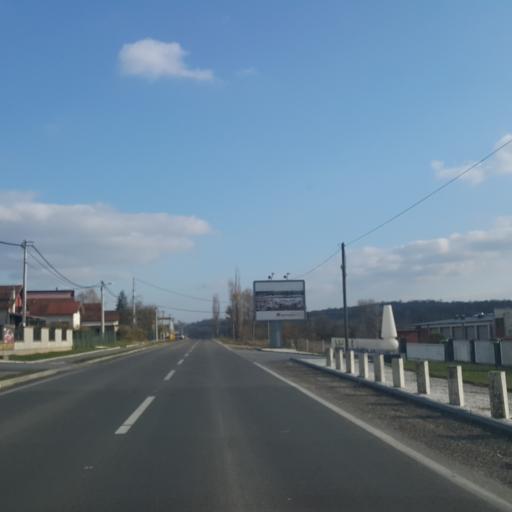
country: RS
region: Central Serbia
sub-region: Sumadijski Okrug
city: Arangelovac
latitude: 44.2929
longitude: 20.6148
